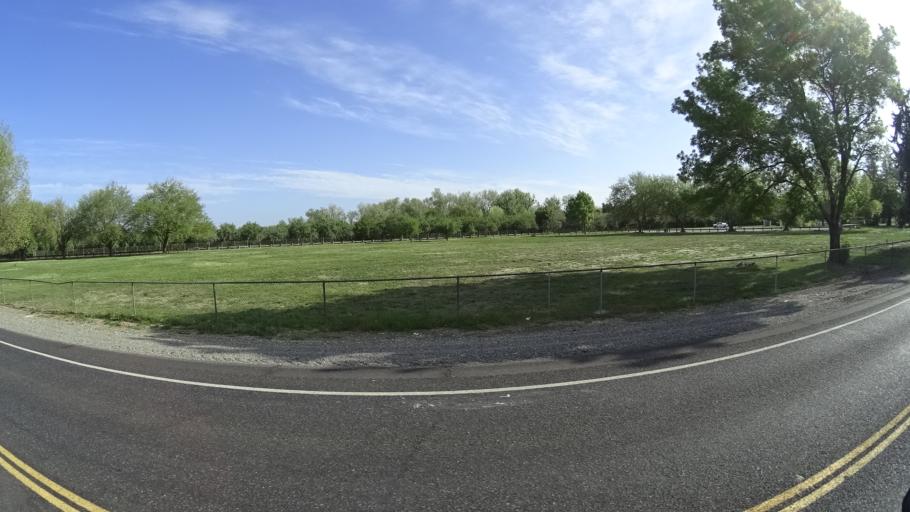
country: US
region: California
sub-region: Glenn County
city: Hamilton City
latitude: 39.6297
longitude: -121.9976
